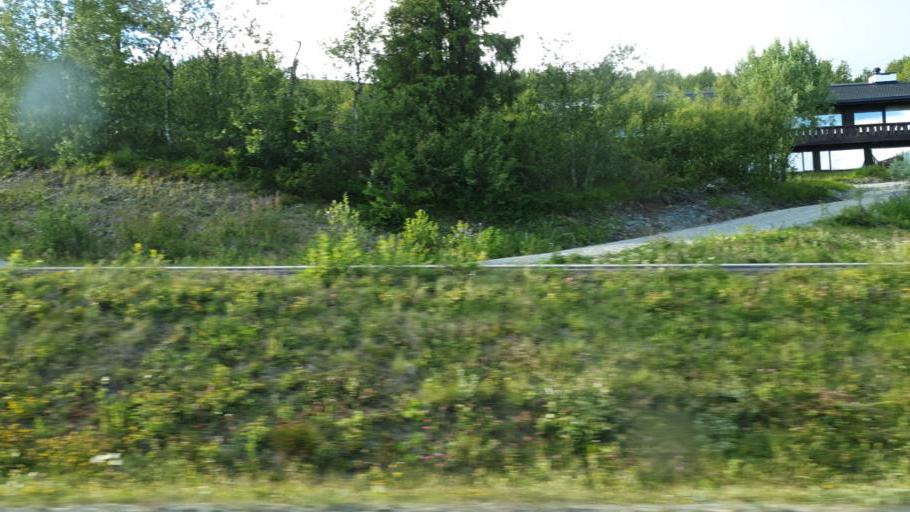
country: NO
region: Oppland
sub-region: Vestre Slidre
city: Slidre
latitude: 61.2501
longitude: 8.8974
